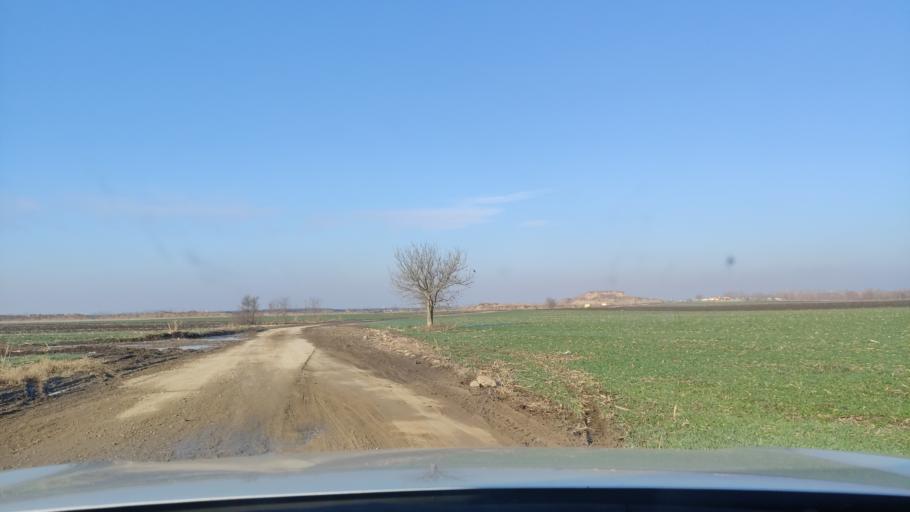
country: RS
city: Ostruznica
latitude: 44.7269
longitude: 20.2853
